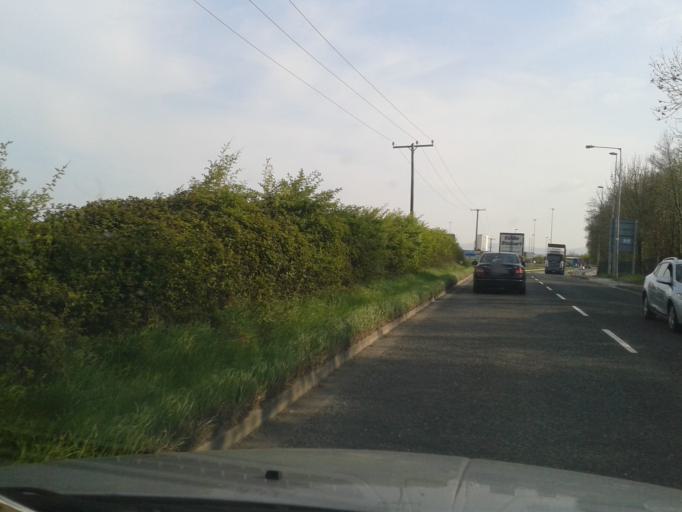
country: IE
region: Leinster
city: Ballymun
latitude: 53.4132
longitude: -6.2652
